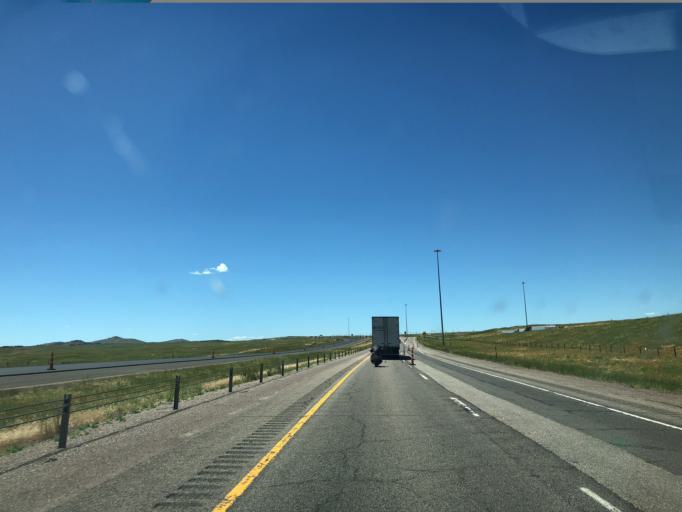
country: US
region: Wyoming
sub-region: Laramie County
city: Cheyenne
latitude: 41.0975
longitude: -105.1088
